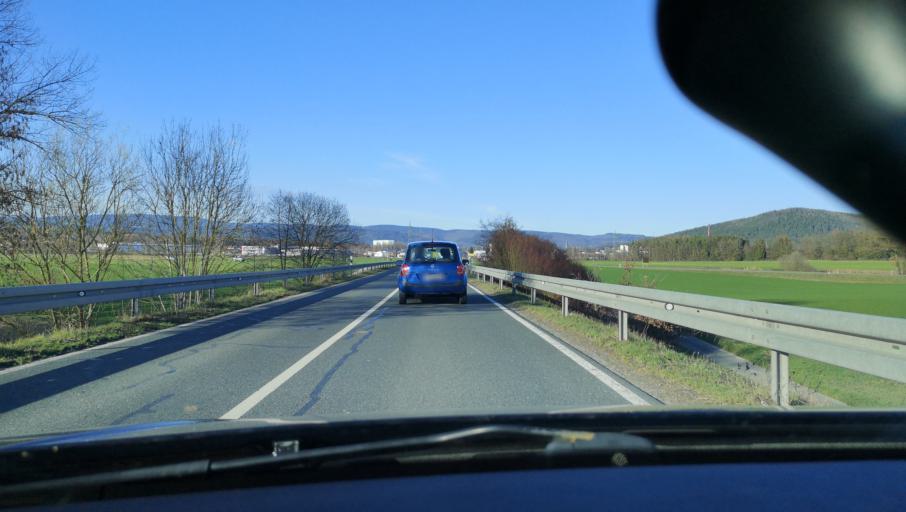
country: DE
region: Bavaria
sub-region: Upper Franconia
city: Neustadt bei Coburg
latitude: 50.3046
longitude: 11.1070
